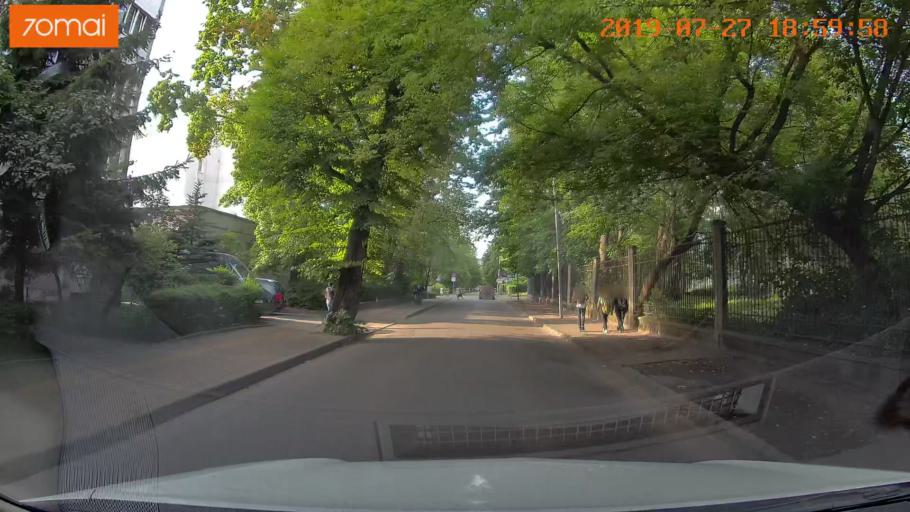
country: RU
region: Kaliningrad
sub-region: Gorod Kaliningrad
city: Kaliningrad
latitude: 54.7251
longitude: 20.4847
